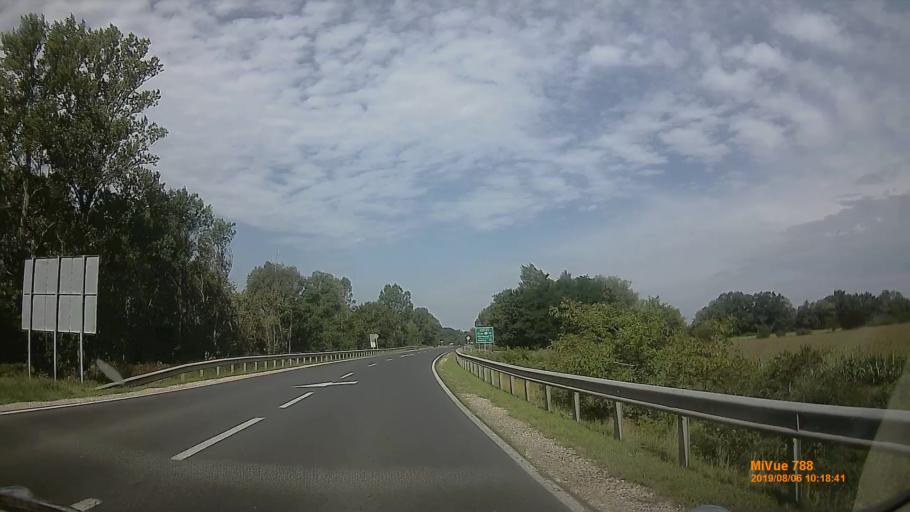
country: HU
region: Vas
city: Vasvar
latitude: 47.0556
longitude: 16.7864
